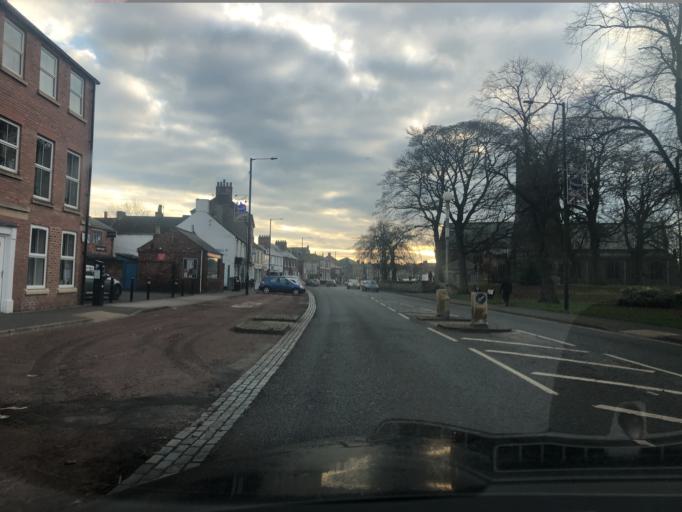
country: GB
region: England
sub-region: North Yorkshire
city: Northallerton
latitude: 54.3432
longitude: -1.4372
